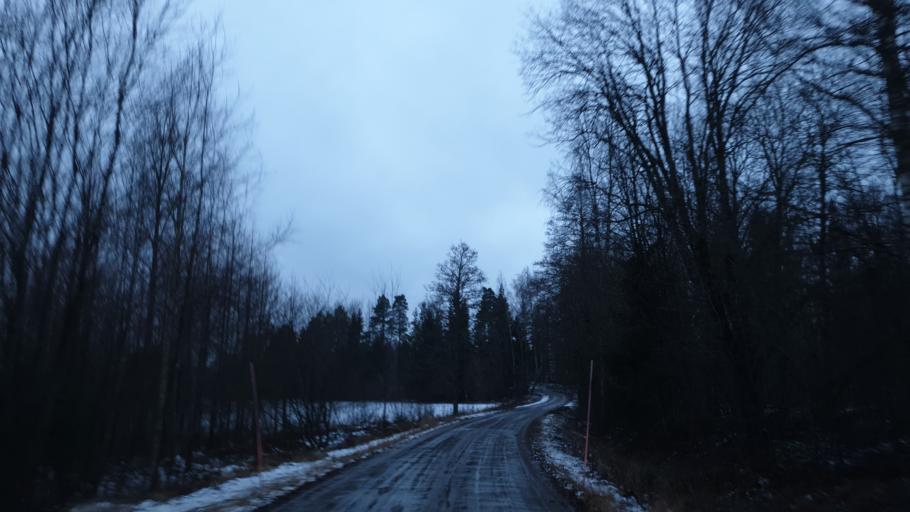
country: SE
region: Uppsala
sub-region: Tierps Kommun
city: Tierp
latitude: 60.3460
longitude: 17.4683
